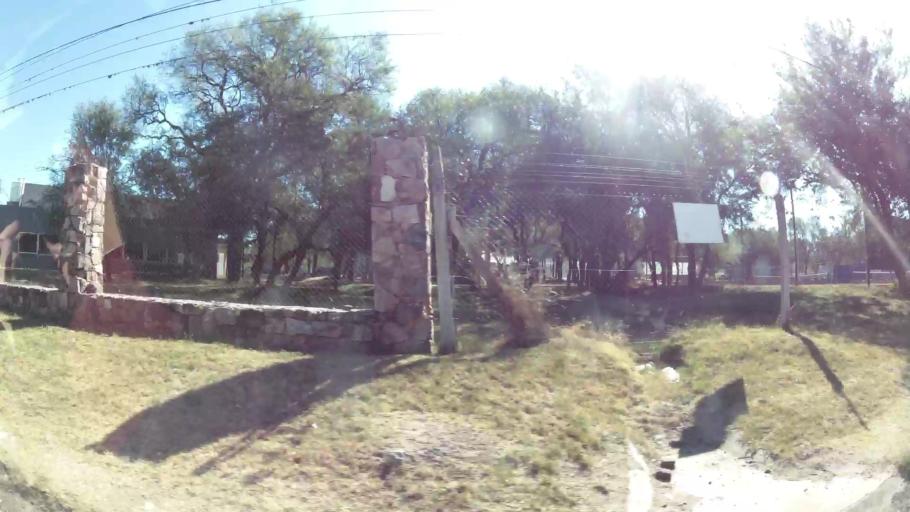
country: AR
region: Cordoba
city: La Calera
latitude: -31.3494
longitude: -64.3101
